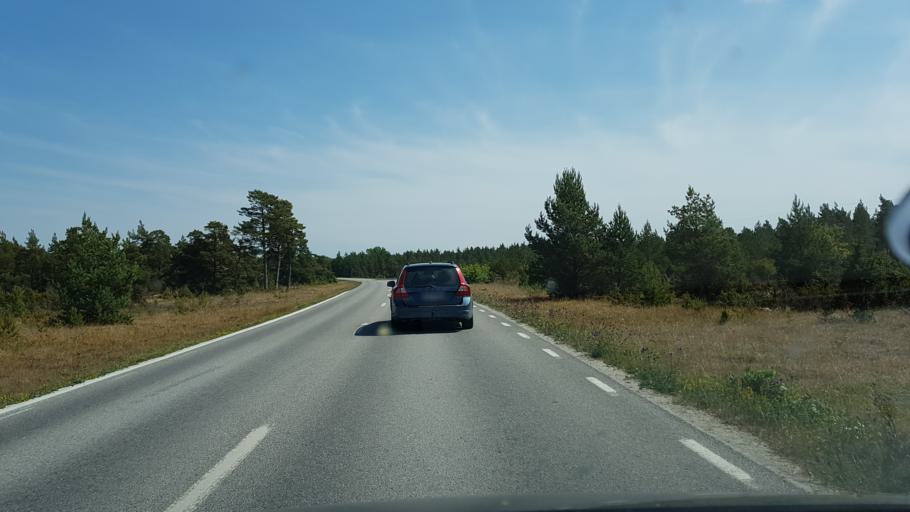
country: SE
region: Gotland
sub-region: Gotland
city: Visby
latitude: 57.6345
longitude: 18.4069
